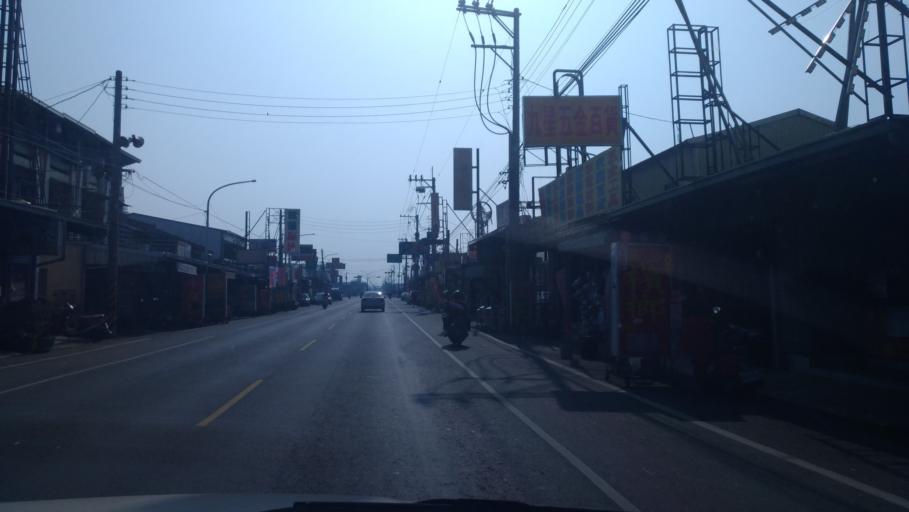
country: TW
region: Taiwan
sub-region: Chiayi
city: Jiayi Shi
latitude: 23.5239
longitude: 120.4223
